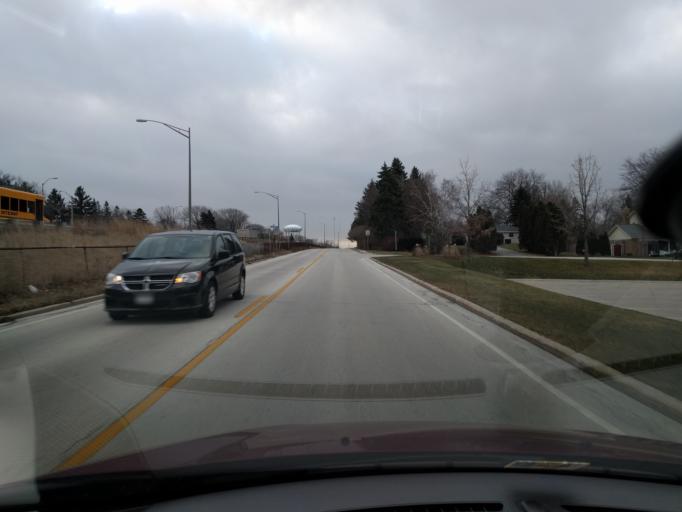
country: US
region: Wisconsin
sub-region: Milwaukee County
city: Glendale
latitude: 43.1386
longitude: -87.9142
